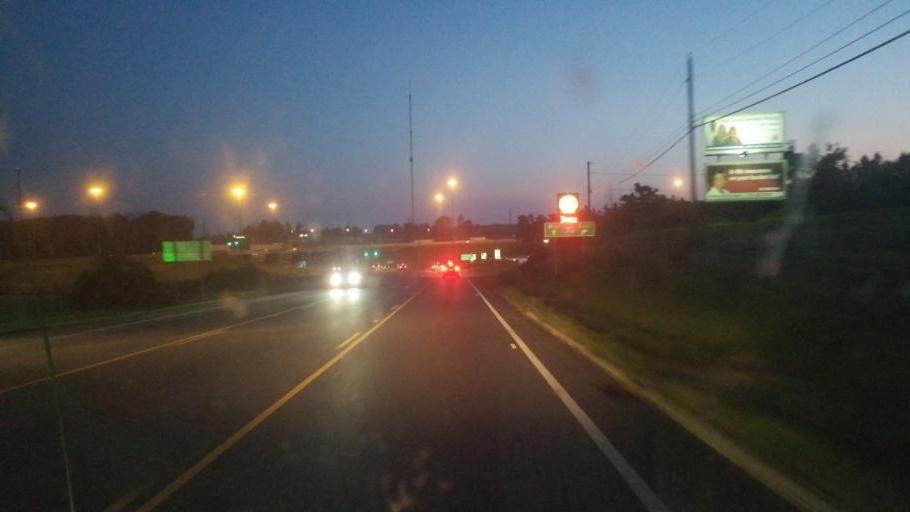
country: US
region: Ohio
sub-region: Perry County
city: Thornport
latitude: 39.9403
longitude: -82.4080
